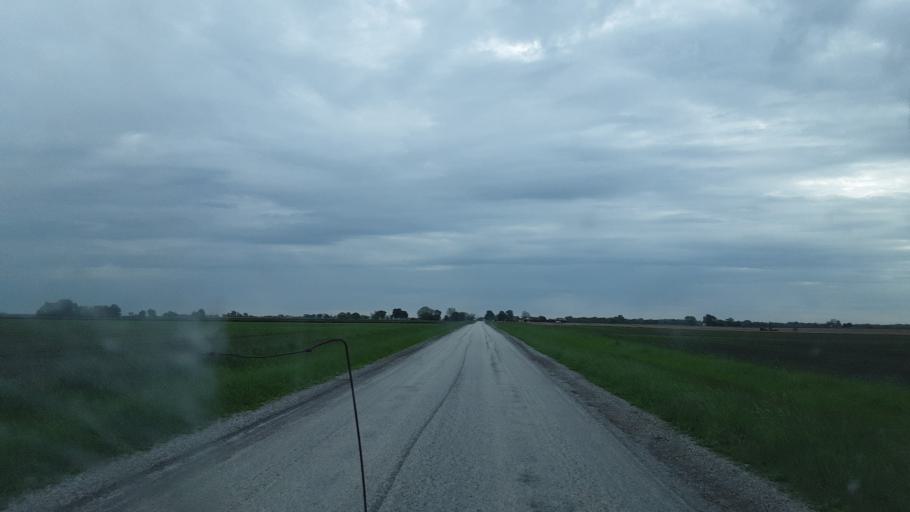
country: US
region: Illinois
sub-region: McDonough County
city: Macomb
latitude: 40.3819
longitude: -90.6706
